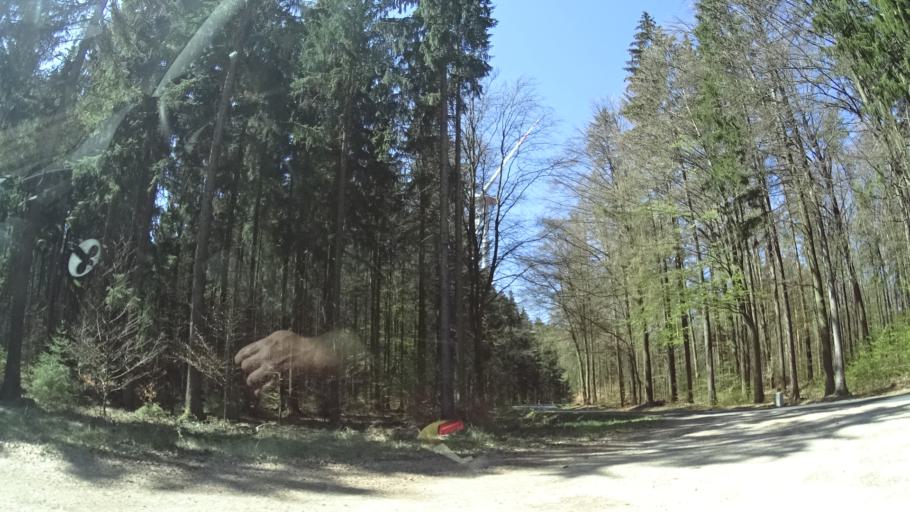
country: DE
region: Bavaria
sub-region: Upper Palatinate
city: Illschwang
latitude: 49.4240
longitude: 11.6674
